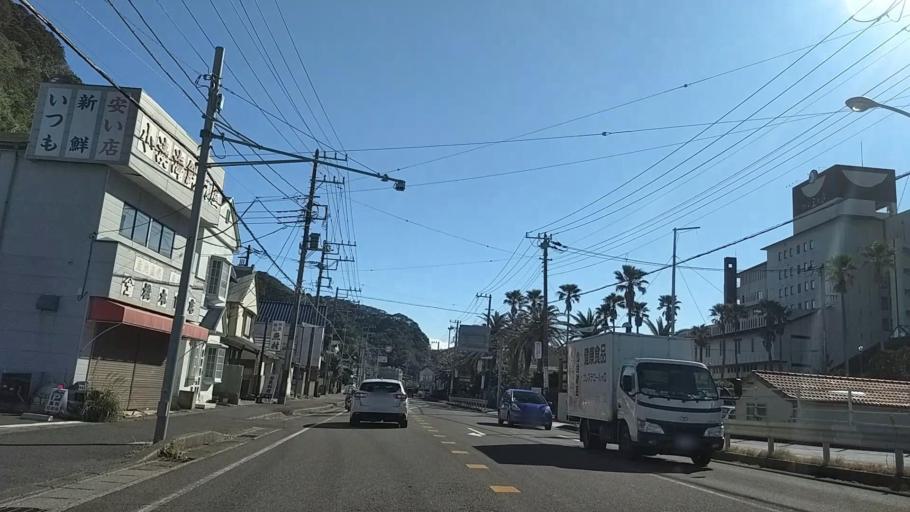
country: JP
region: Chiba
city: Kawaguchi
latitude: 35.1252
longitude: 140.1947
